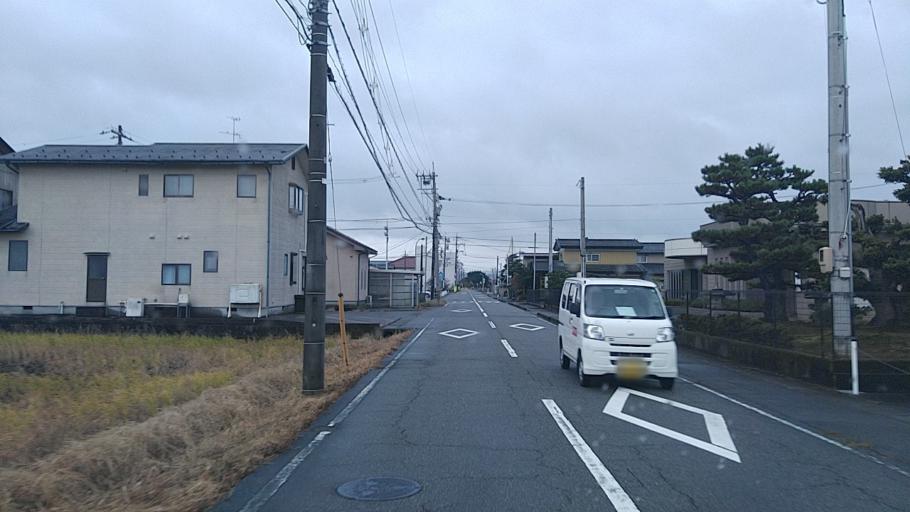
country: JP
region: Ishikawa
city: Komatsu
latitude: 36.3304
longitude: 136.3807
